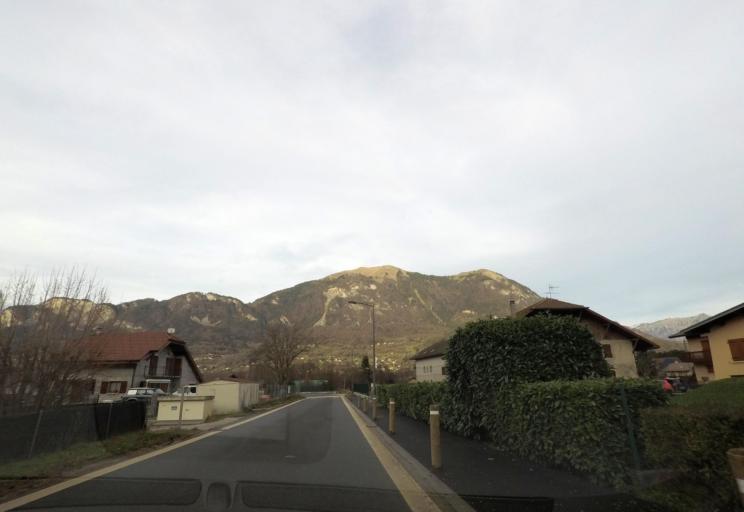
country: FR
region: Rhone-Alpes
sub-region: Departement de la Haute-Savoie
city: Ayse
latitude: 46.0673
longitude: 6.4421
